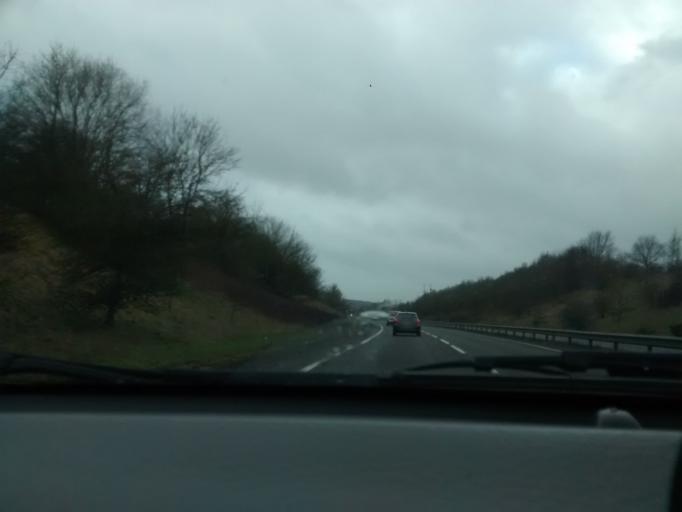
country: GB
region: England
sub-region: Suffolk
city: Stowmarket
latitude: 52.1963
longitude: 1.0068
